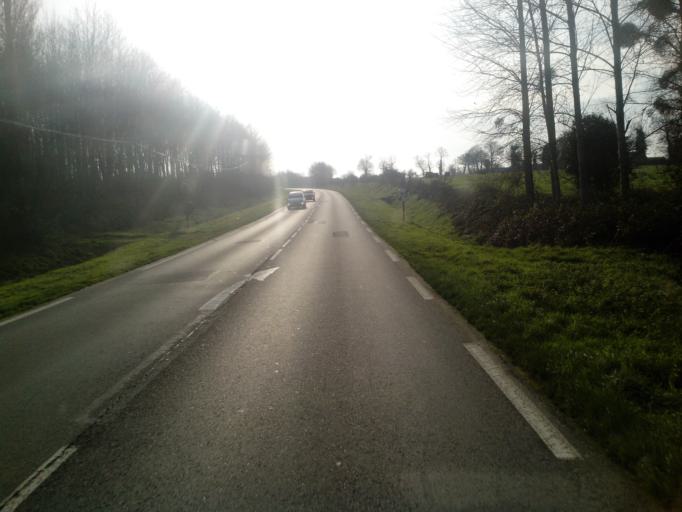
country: FR
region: Brittany
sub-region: Departement d'Ille-et-Vilaine
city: Saint-Meen-le-Grand
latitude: 48.1732
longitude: -2.2061
